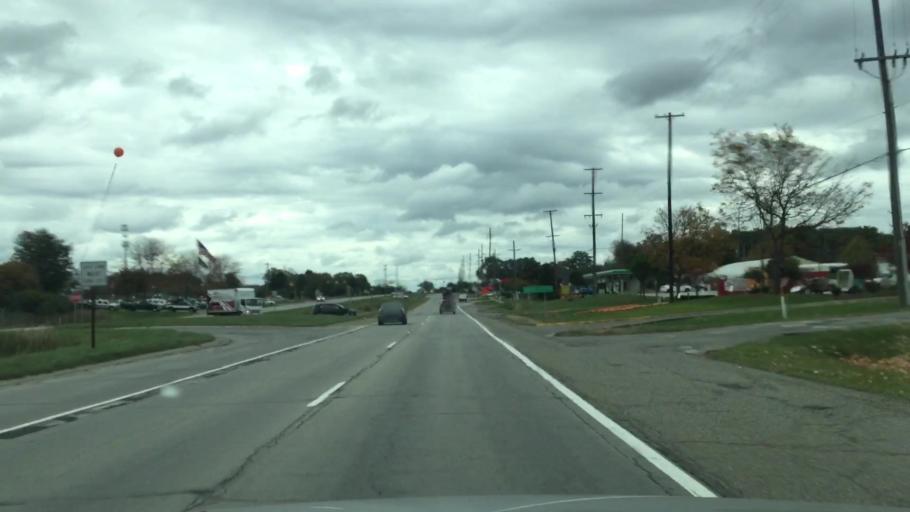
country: US
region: Michigan
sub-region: Oakland County
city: Milford
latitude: 42.6360
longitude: -83.6656
